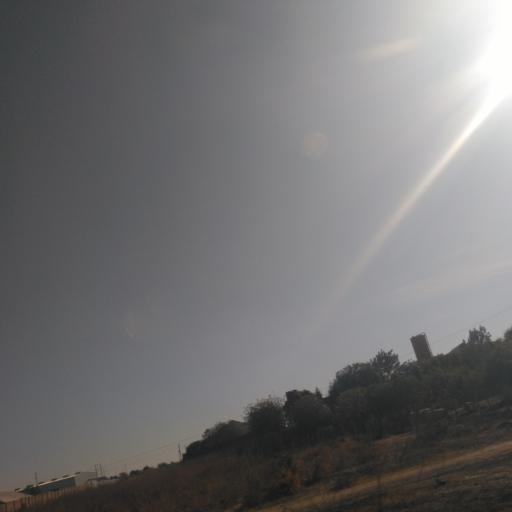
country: TZ
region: Dodoma
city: Dodoma
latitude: -6.1557
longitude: 35.7098
